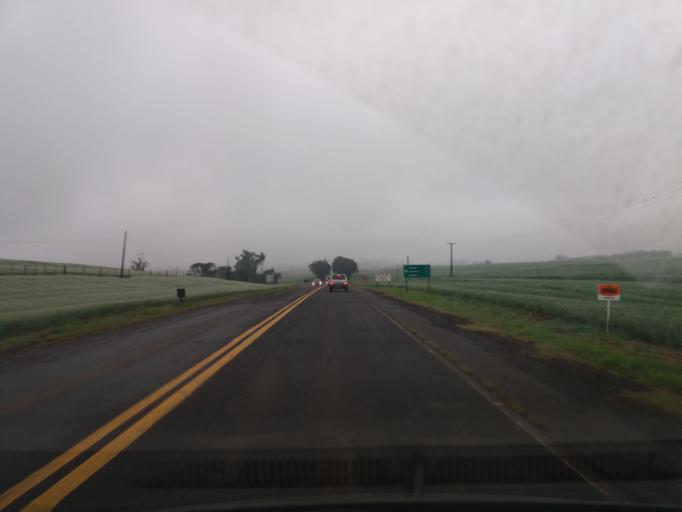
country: BR
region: Parana
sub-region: Realeza
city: Realeza
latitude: -25.8094
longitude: -53.5211
